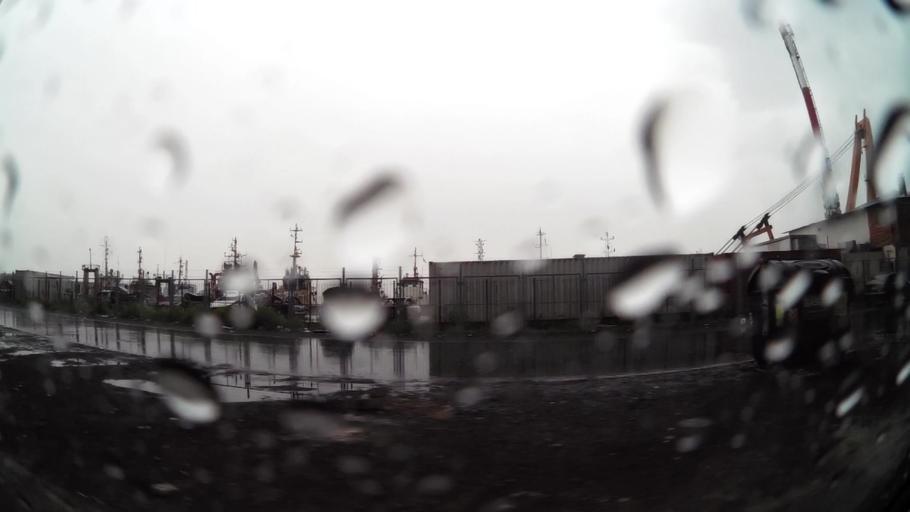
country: AR
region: Buenos Aires
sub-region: Partido de Avellaneda
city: Avellaneda
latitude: -34.6337
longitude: -58.3534
